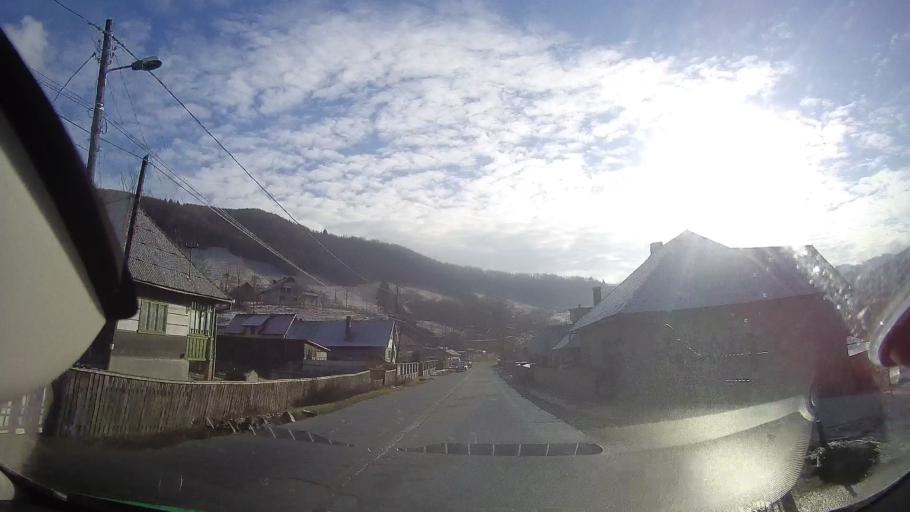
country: RO
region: Alba
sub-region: Comuna Sohodol
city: Sohodol
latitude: 46.3698
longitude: 23.0257
